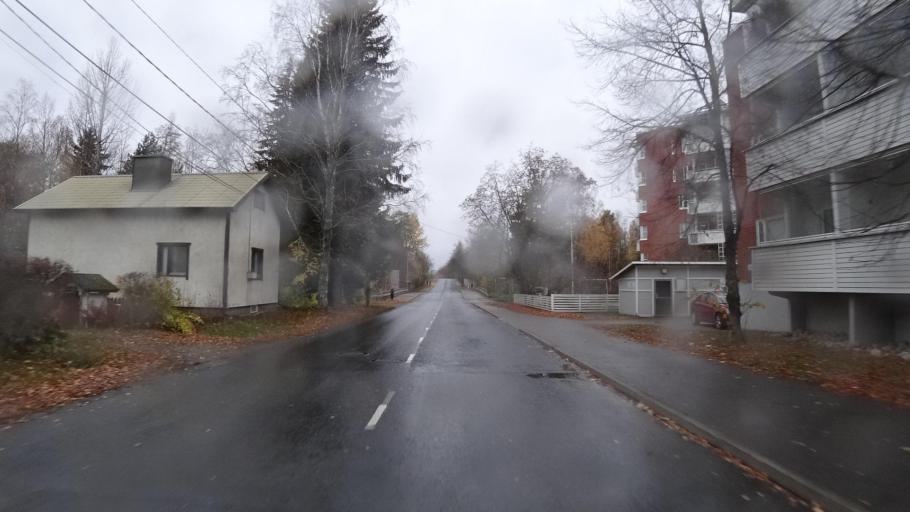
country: FI
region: Northern Savo
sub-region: Kuopio
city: Kuopio
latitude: 62.8978
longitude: 27.7150
